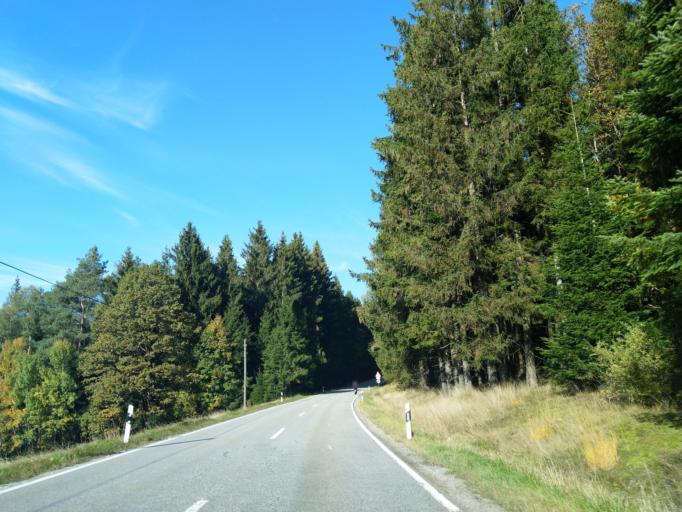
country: DE
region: Bavaria
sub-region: Lower Bavaria
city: Achslach
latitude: 48.9611
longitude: 12.9274
